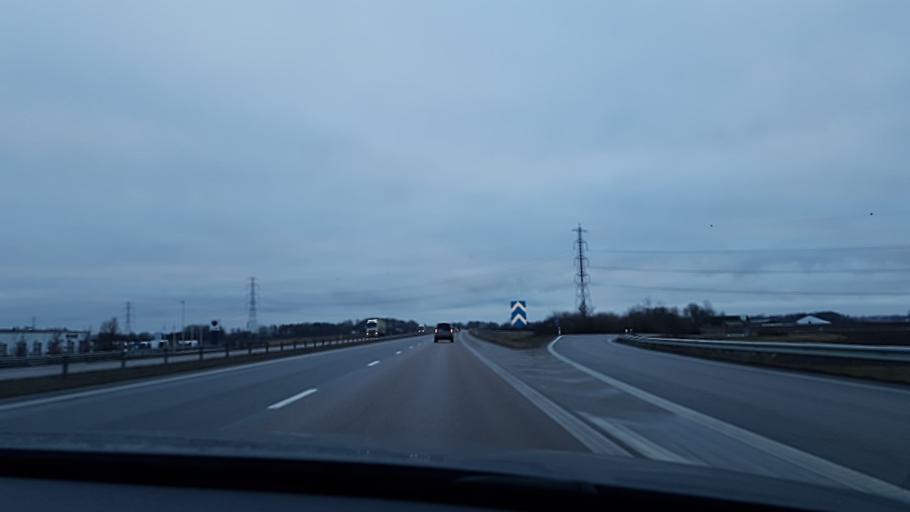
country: SE
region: Skane
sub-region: Astorps Kommun
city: Kvidinge
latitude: 56.1921
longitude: 13.0578
